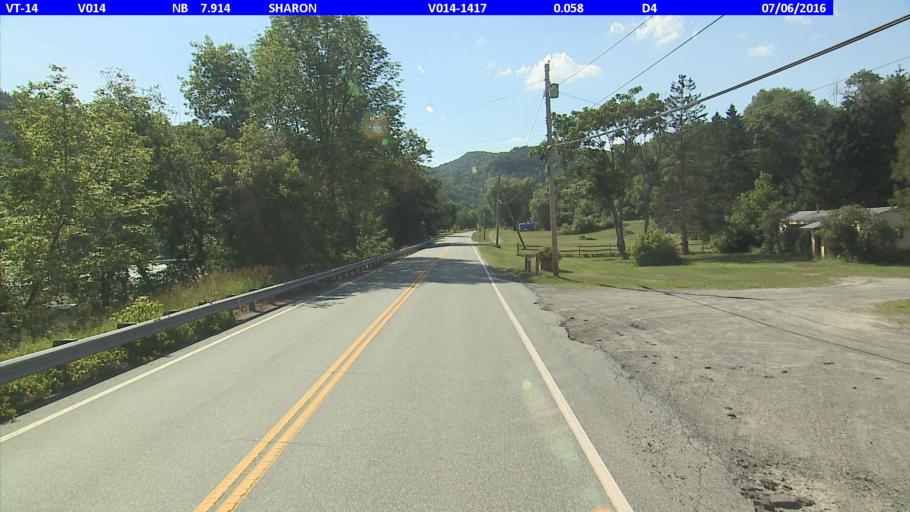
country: US
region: Vermont
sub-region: Windsor County
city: Wilder
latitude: 43.7229
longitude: -72.4269
